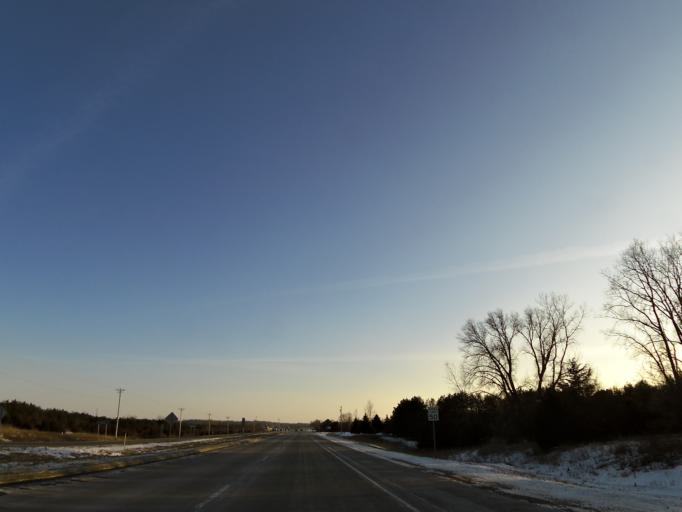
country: US
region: Wisconsin
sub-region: Saint Croix County
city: Hudson
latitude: 44.9768
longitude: -92.6802
